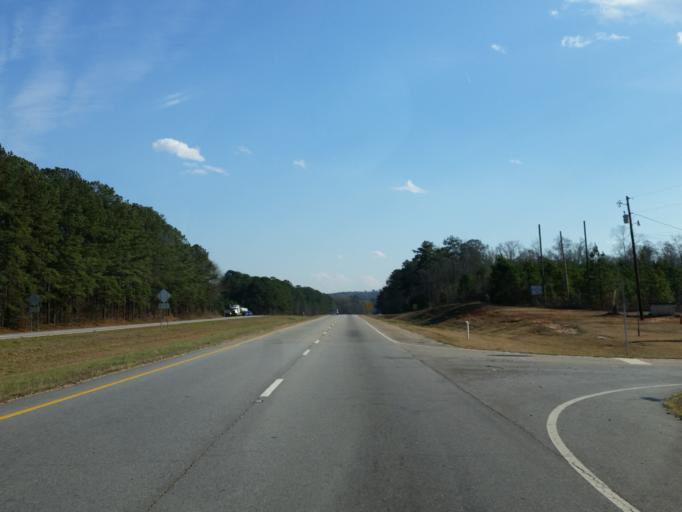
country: US
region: Georgia
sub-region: Lamar County
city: Barnesville
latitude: 33.0917
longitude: -84.1763
